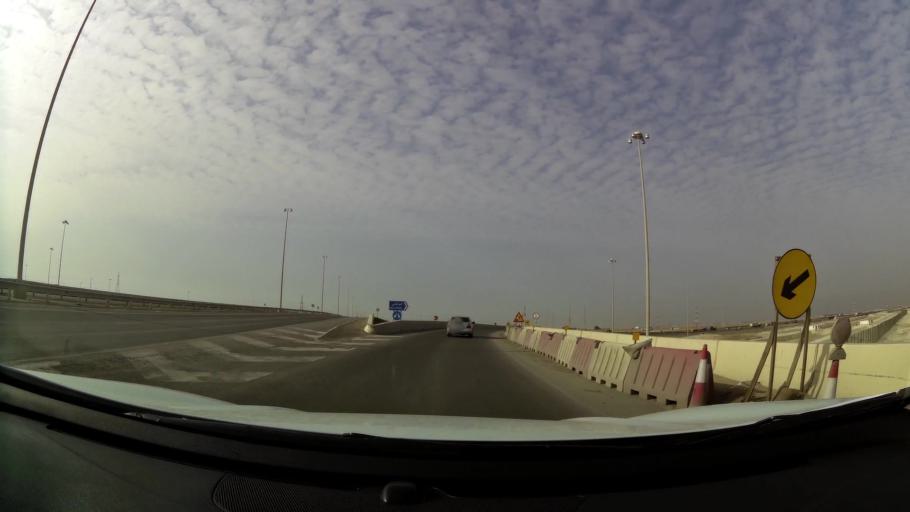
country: AE
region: Abu Dhabi
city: Abu Dhabi
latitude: 24.2112
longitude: 54.4161
